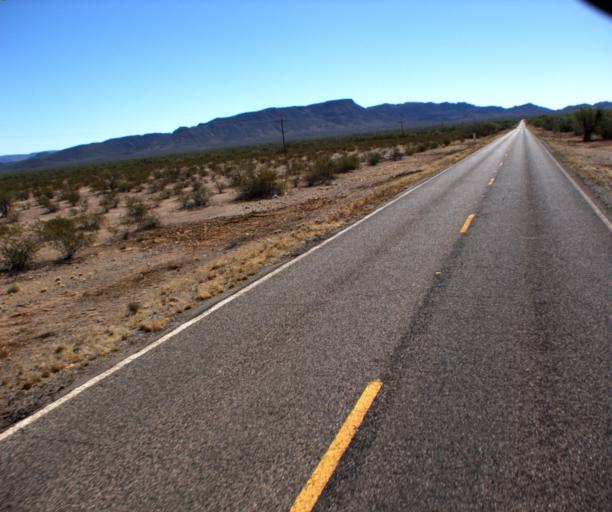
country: US
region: Arizona
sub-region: Pima County
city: Ajo
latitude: 32.3349
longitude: -112.7914
